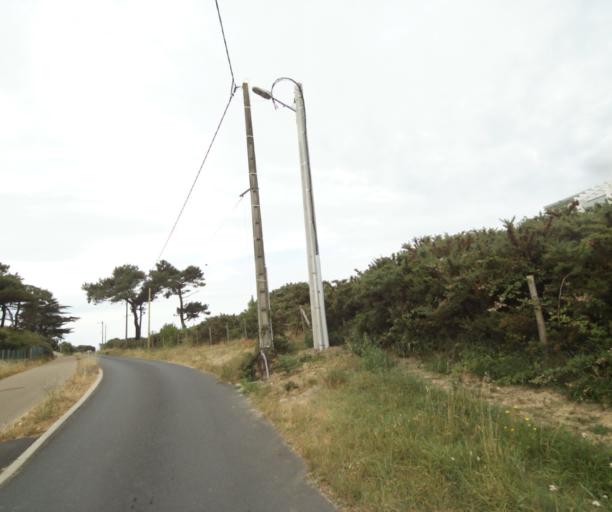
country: FR
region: Pays de la Loire
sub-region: Departement de la Vendee
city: Chateau-d'Olonne
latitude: 46.4735
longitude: -1.7418
